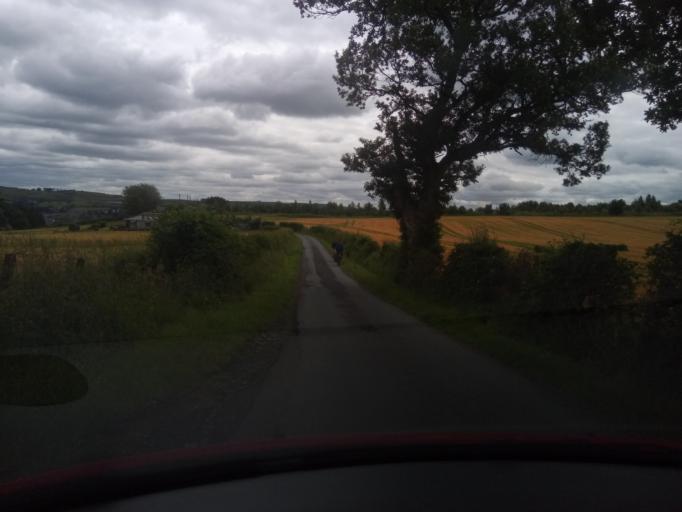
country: GB
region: Scotland
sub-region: The Scottish Borders
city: Hawick
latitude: 55.4242
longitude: -2.8128
